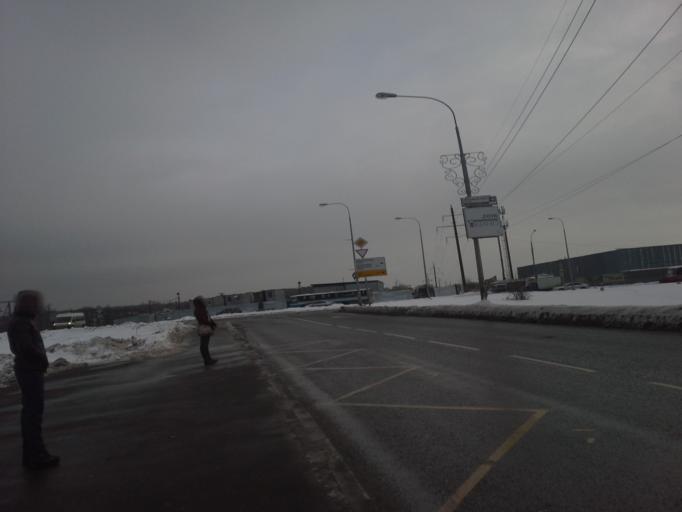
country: RU
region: Moskovskaya
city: Kommunarka
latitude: 55.5724
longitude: 37.4949
